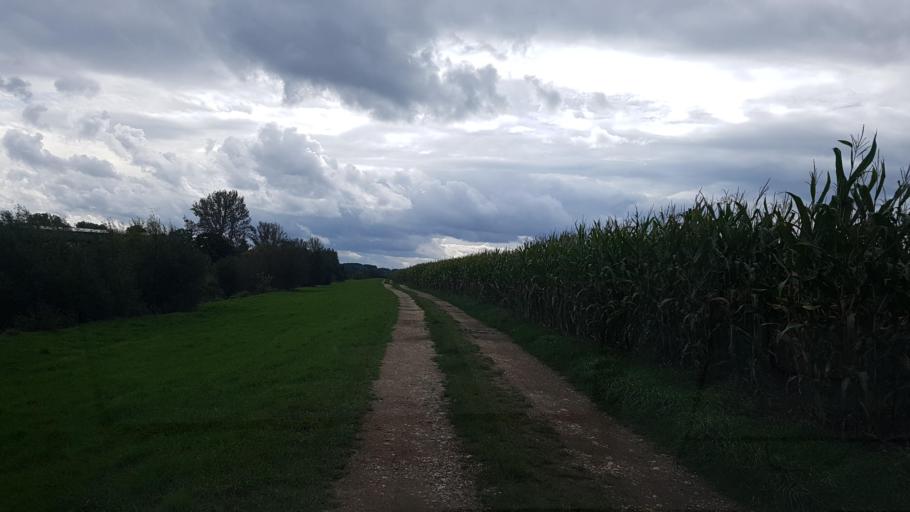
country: DE
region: Saxony
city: Pegau
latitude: 51.1472
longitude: 12.2564
